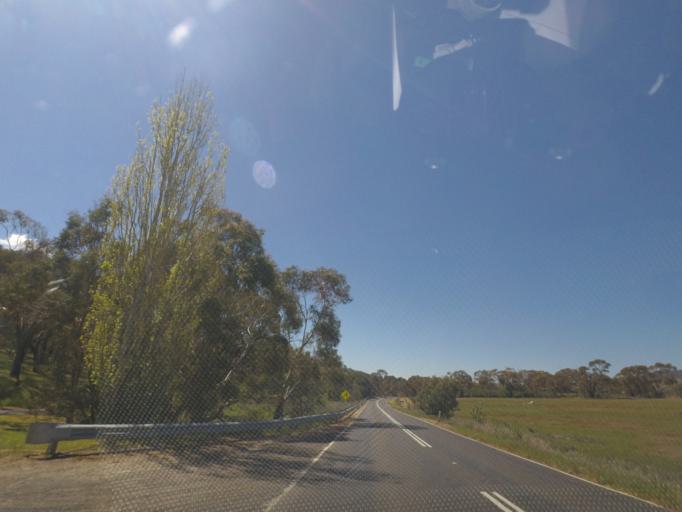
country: AU
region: Victoria
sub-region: Hume
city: Sunbury
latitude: -37.0570
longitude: 144.7840
